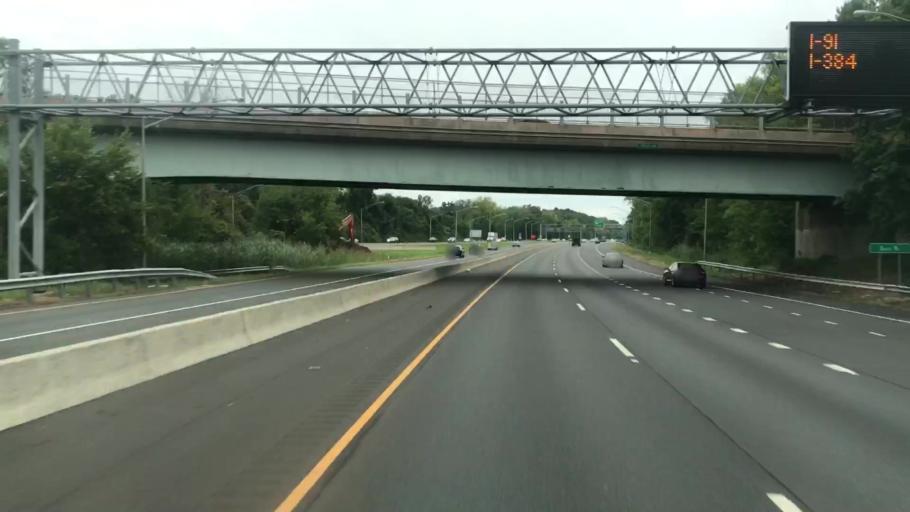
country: US
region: Connecticut
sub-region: Hartford County
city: Farmington
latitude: 41.7207
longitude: -72.7901
